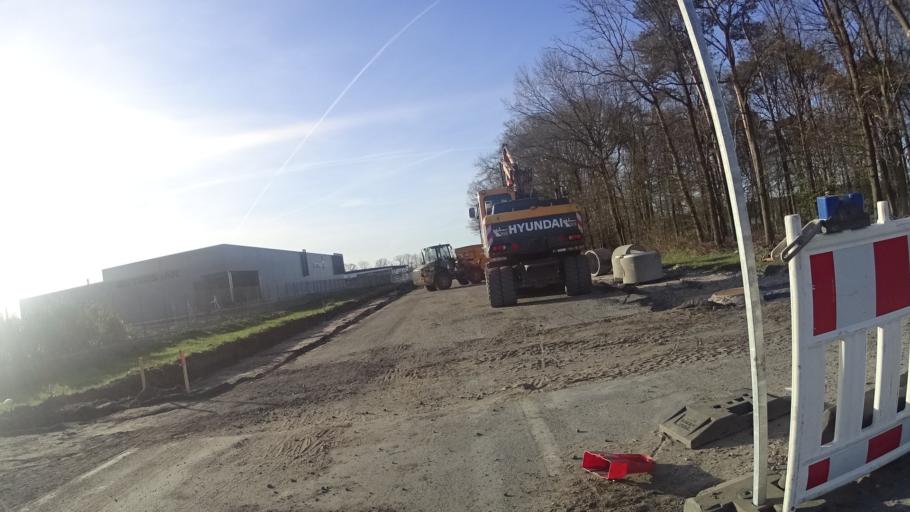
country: DE
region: North Rhine-Westphalia
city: Emsdetten
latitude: 52.1425
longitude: 7.5372
